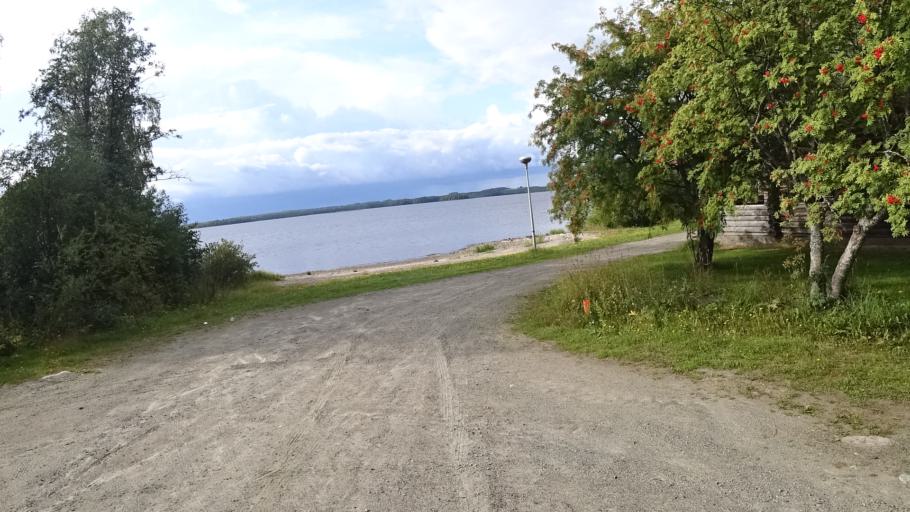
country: FI
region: North Karelia
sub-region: Joensuu
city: Ilomantsi
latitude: 62.6768
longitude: 30.9118
